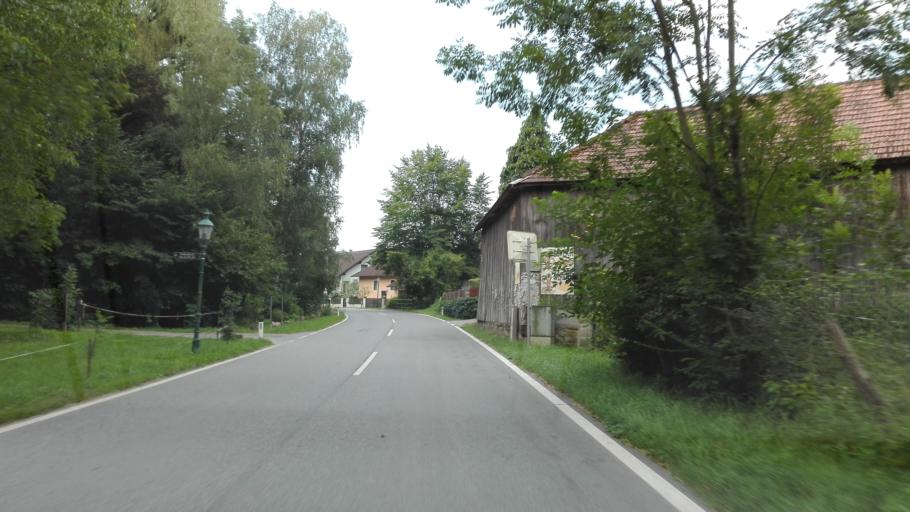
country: AT
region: Lower Austria
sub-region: Politischer Bezirk Sankt Polten
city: Kasten bei Boheimkirchen
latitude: 48.1401
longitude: 15.7444
